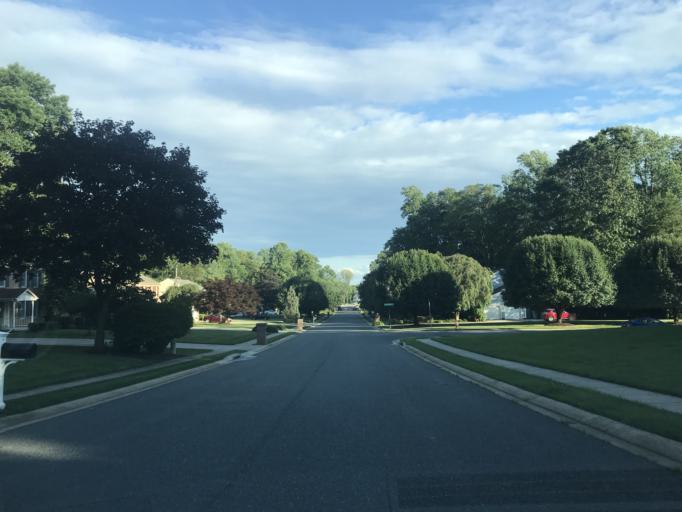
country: US
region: Maryland
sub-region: Harford County
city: South Bel Air
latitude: 39.5606
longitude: -76.3145
